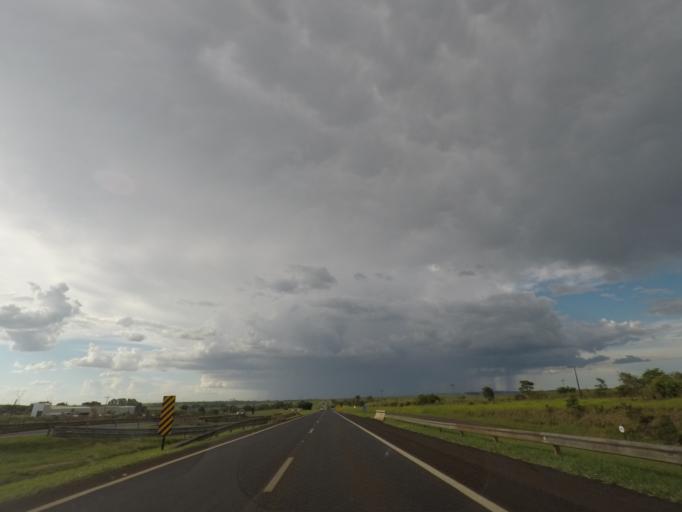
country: BR
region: Sao Paulo
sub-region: Jardinopolis
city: Jardinopolis
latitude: -21.0342
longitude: -47.8333
